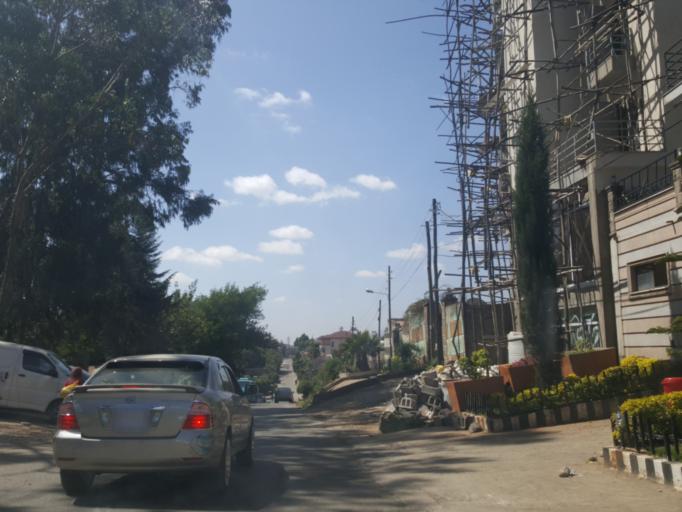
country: ET
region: Adis Abeba
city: Addis Ababa
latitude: 9.0571
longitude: 38.7381
